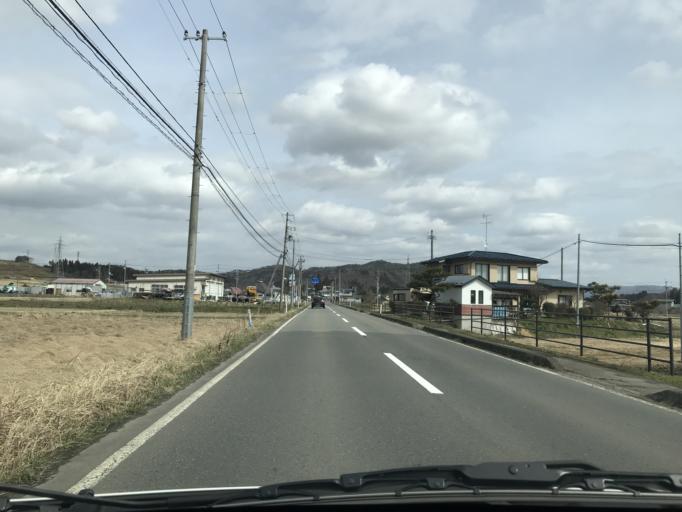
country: JP
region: Iwate
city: Mizusawa
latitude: 39.2015
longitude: 141.1882
